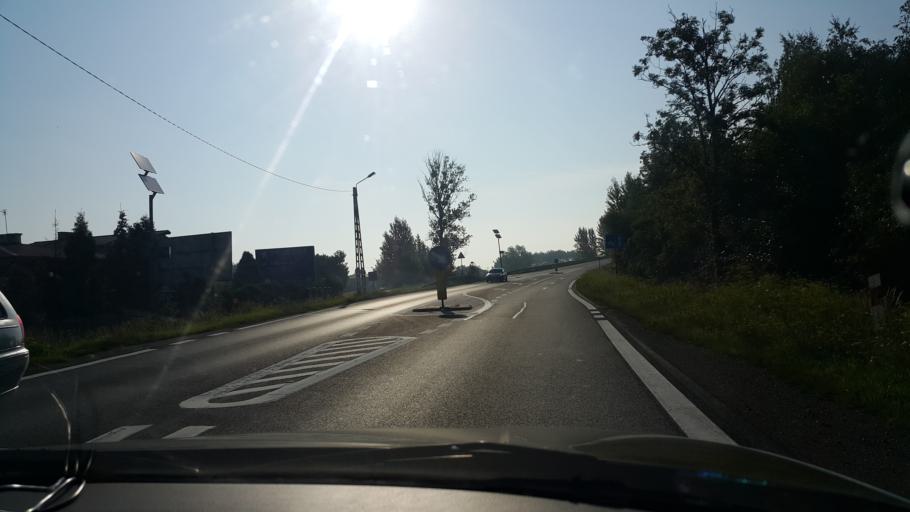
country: PL
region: Masovian Voivodeship
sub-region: Powiat radomski
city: Jastrzebia
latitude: 51.4132
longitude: 21.2325
